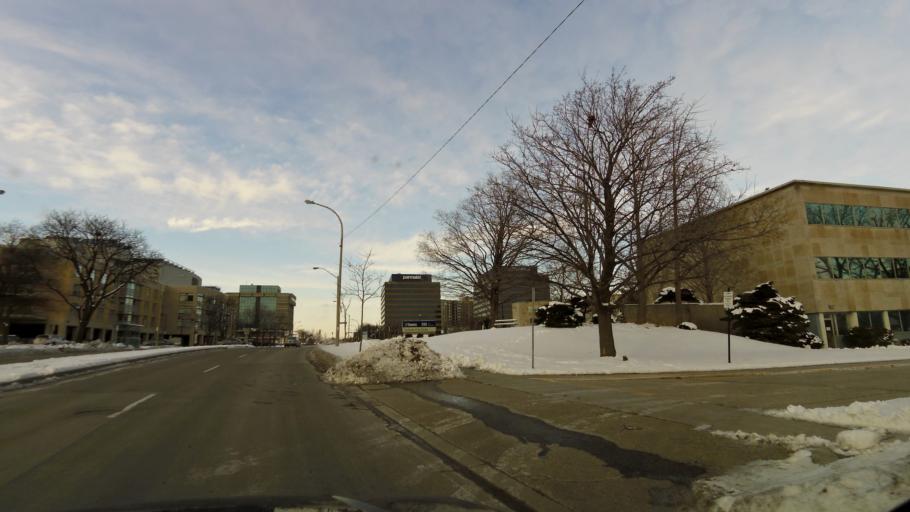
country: CA
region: Ontario
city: Etobicoke
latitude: 43.6427
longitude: -79.5662
